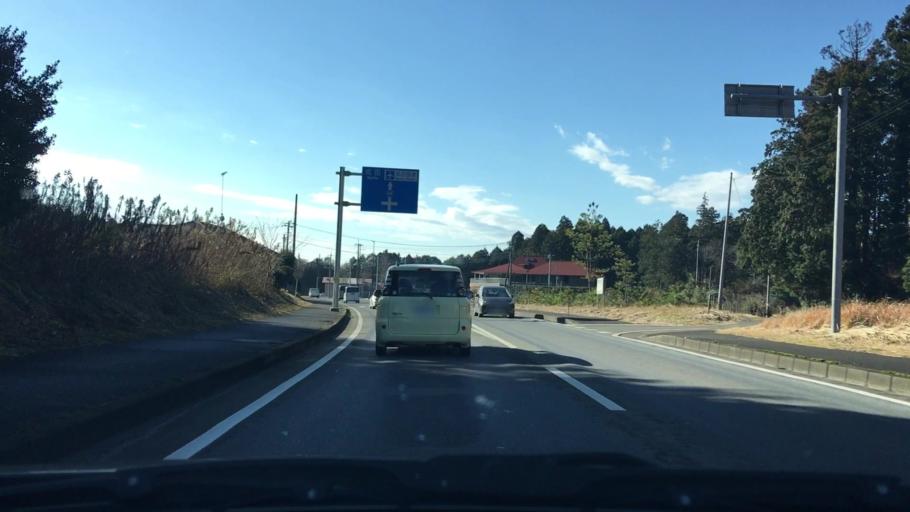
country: JP
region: Chiba
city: Sawara
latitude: 35.8040
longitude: 140.4683
